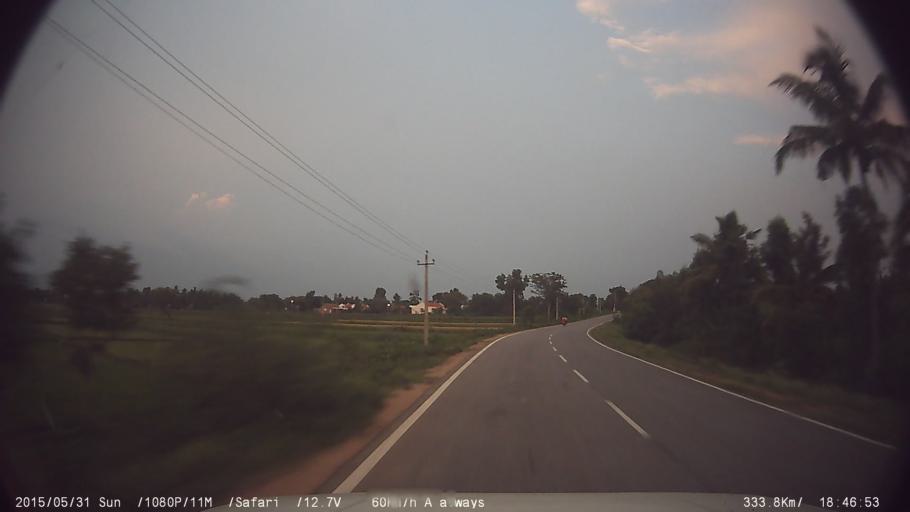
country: IN
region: Karnataka
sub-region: Mysore
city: Tirumakudal Narsipur
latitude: 12.1628
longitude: 76.8368
